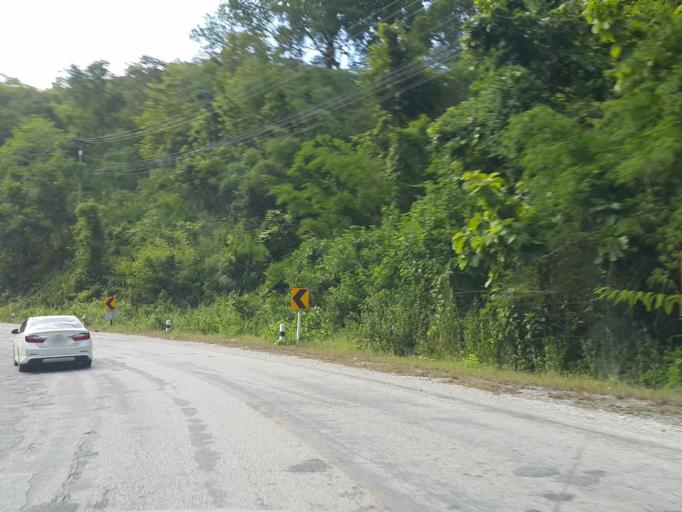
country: TH
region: Lampang
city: Thoen
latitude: 17.6370
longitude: 99.3105
